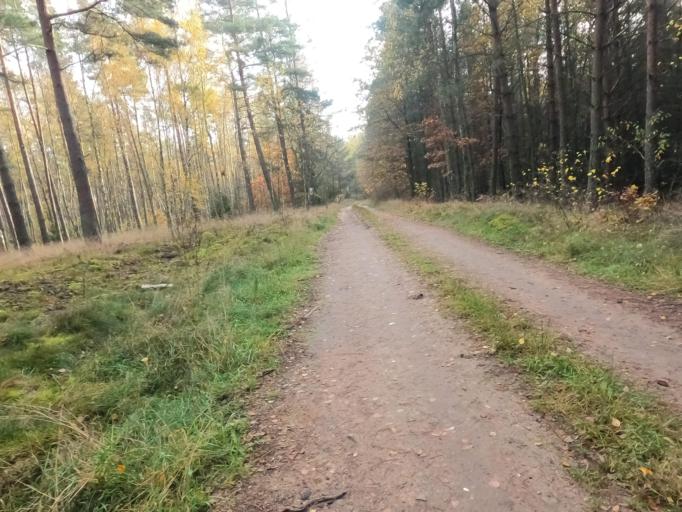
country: PL
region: West Pomeranian Voivodeship
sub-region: Powiat szczecinecki
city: Lubowo
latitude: 53.5514
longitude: 16.4237
